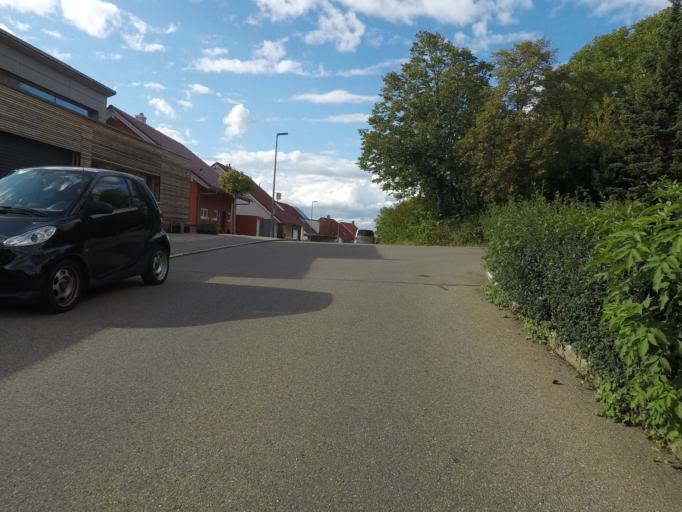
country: DE
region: Baden-Wuerttemberg
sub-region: Tuebingen Region
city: Pfullingen
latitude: 48.4613
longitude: 9.2327
